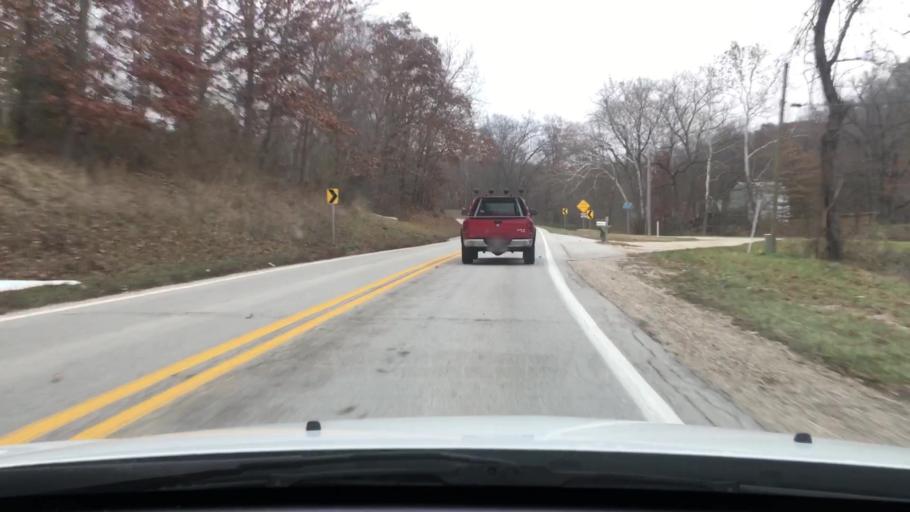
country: US
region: Missouri
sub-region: Pike County
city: Louisiana
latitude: 39.5190
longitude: -90.9518
